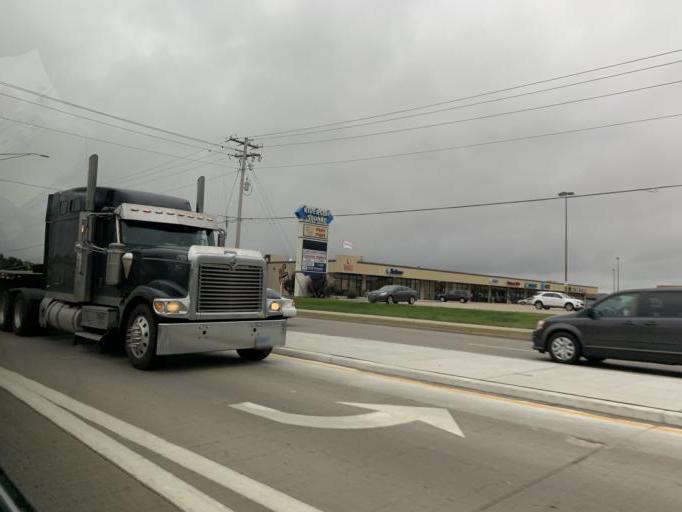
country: US
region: Wisconsin
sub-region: Crawford County
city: Prairie du Chien
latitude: 43.0273
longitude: -91.1258
